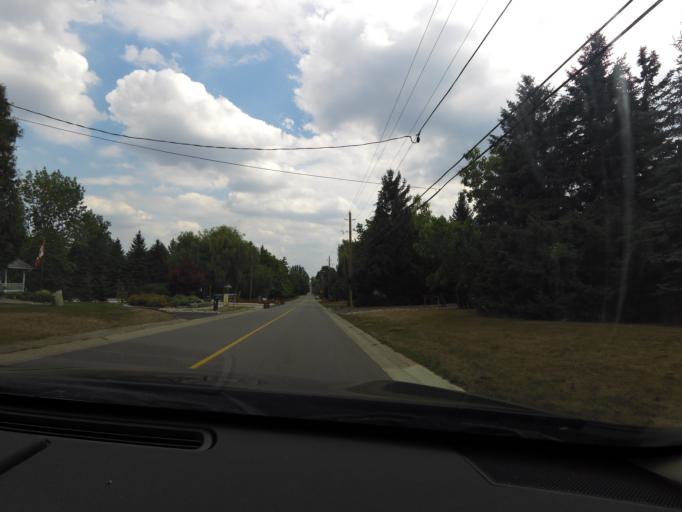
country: CA
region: Ontario
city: Brampton
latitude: 43.7580
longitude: -79.9296
